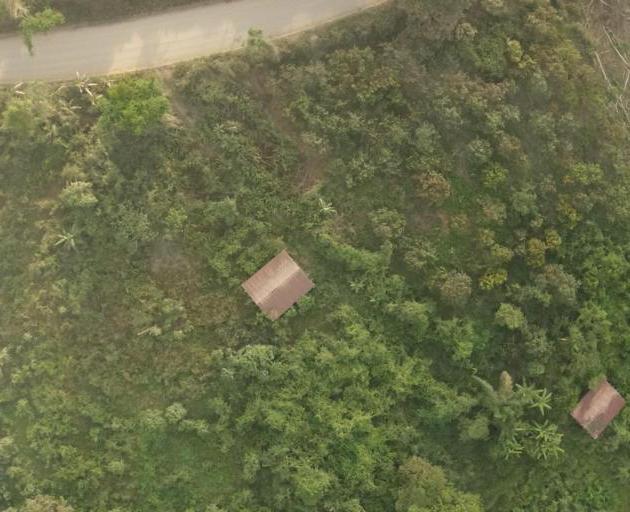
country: BO
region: La Paz
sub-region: Provincia Larecaja
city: Guanay
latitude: -15.7734
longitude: -67.6589
